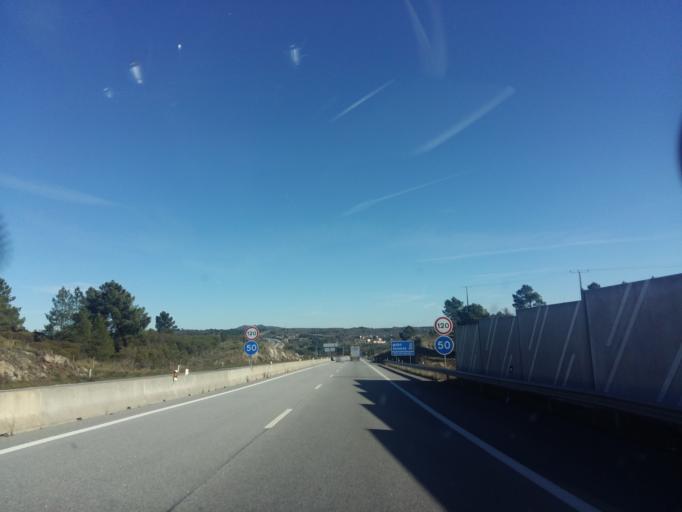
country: PT
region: Guarda
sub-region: Guarda
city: Sequeira
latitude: 40.5731
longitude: -7.2038
